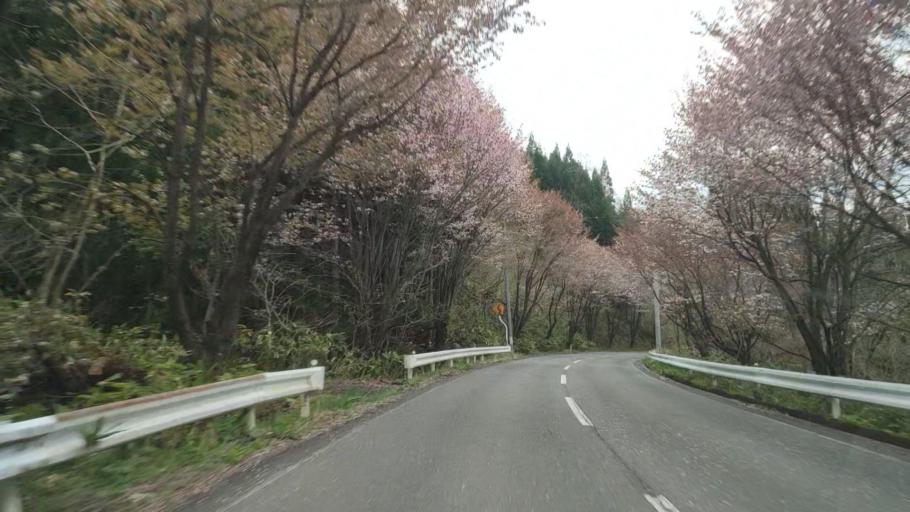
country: JP
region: Akita
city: Hanawa
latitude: 40.3629
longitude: 140.7864
